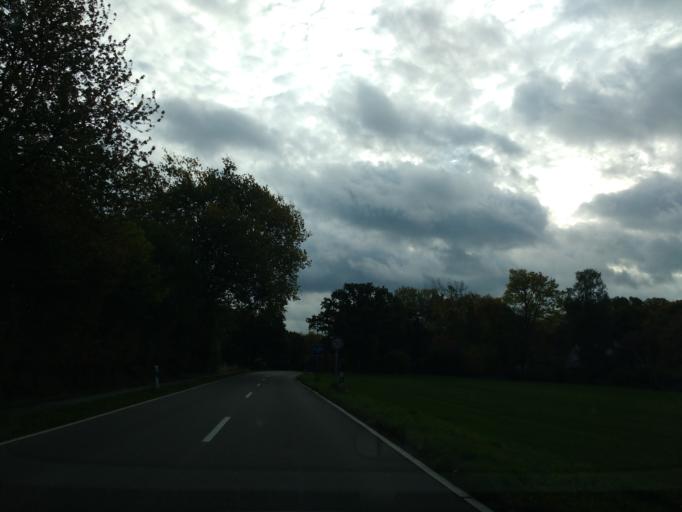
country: DE
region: Schleswig-Holstein
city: Travemuende
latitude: 53.9721
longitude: 10.8536
